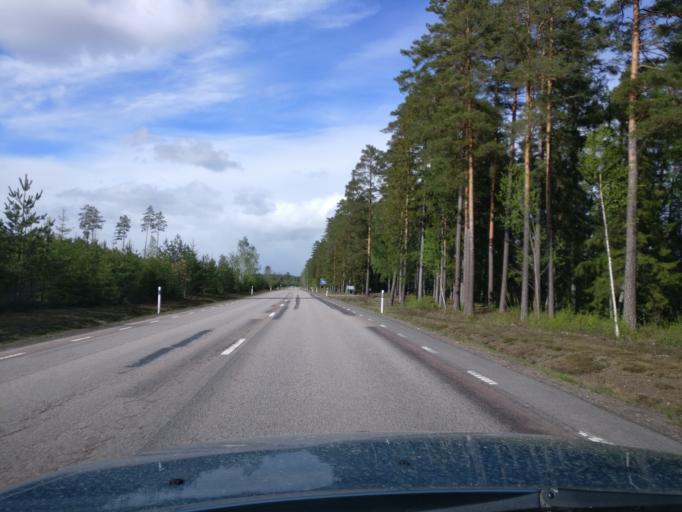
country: SE
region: Vaermland
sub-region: Forshaga Kommun
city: Forshaga
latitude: 59.5000
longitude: 13.4335
